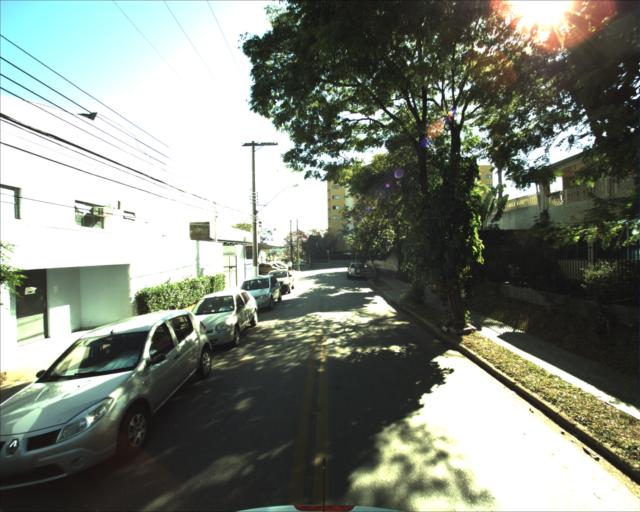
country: BR
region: Sao Paulo
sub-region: Sorocaba
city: Sorocaba
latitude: -23.4784
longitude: -47.4366
